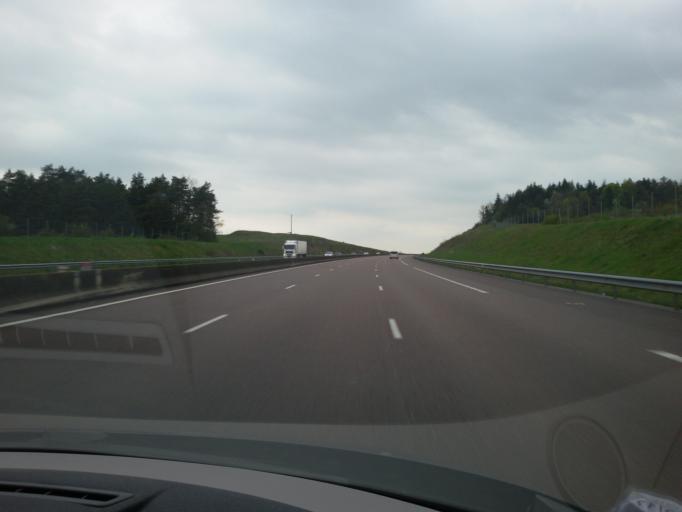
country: FR
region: Champagne-Ardenne
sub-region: Departement de la Haute-Marne
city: Rolampont
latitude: 47.8701
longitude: 5.2203
